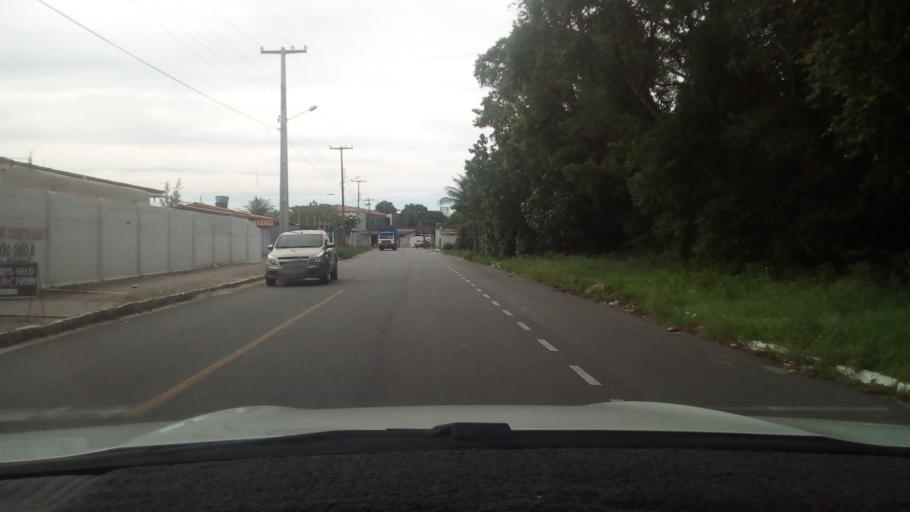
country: BR
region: Paraiba
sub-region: Joao Pessoa
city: Joao Pessoa
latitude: -7.1605
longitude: -34.8654
